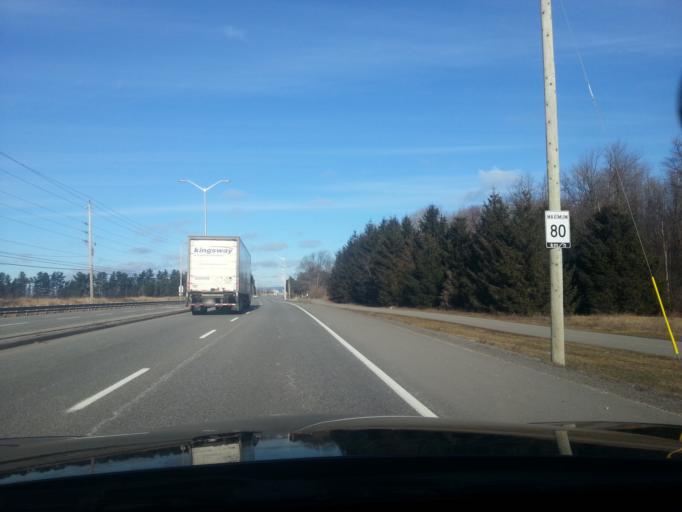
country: CA
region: Ontario
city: Bells Corners
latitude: 45.3177
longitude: -75.7420
